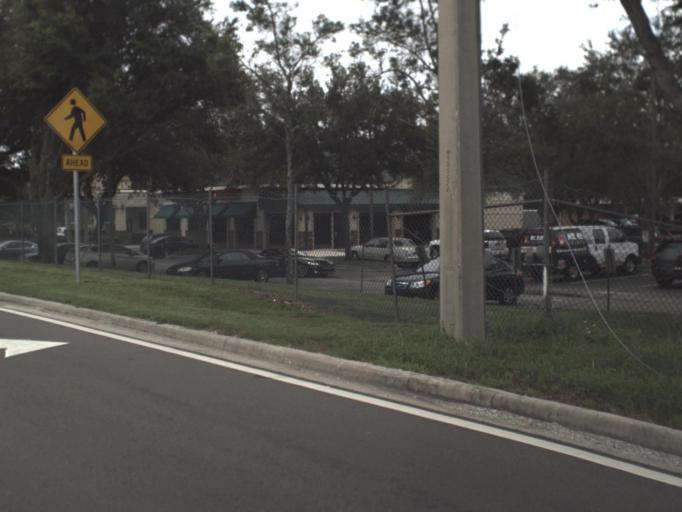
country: US
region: Florida
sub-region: Sarasota County
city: Lake Sarasota
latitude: 27.2990
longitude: -82.4502
